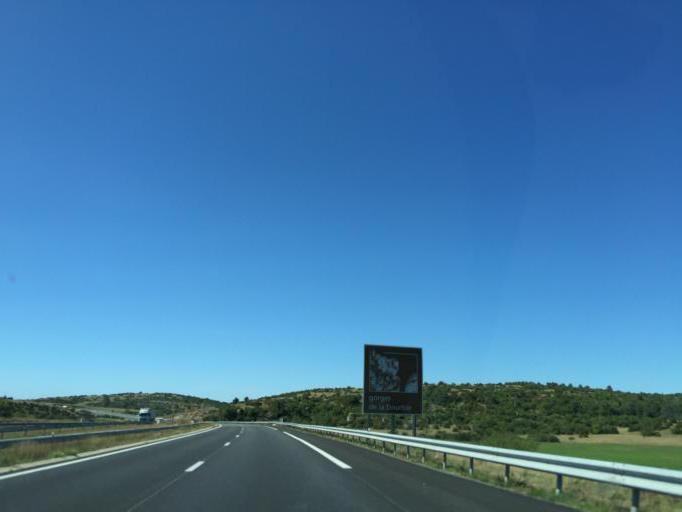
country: FR
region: Midi-Pyrenees
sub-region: Departement de l'Aveyron
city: La Cavalerie
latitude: 43.9021
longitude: 3.2778
